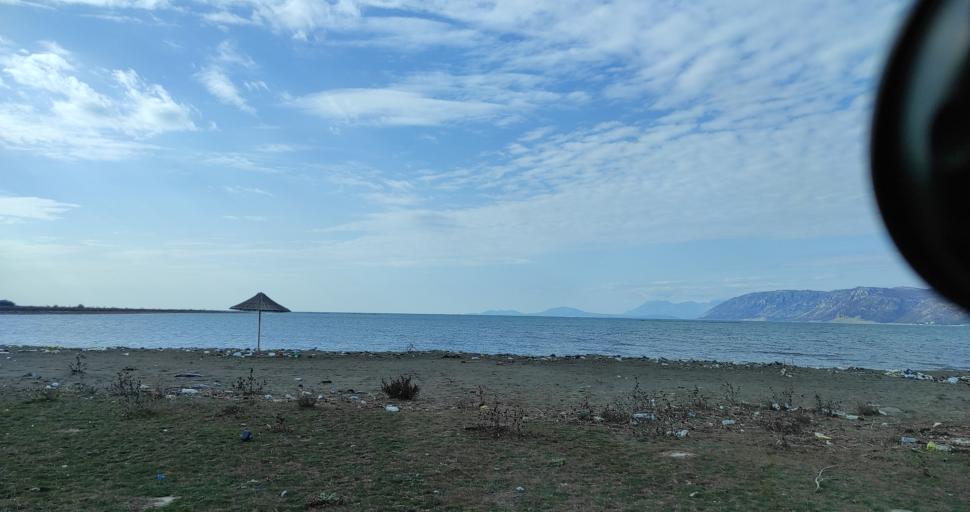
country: AL
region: Lezhe
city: Shengjin
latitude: 41.7682
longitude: 19.5989
